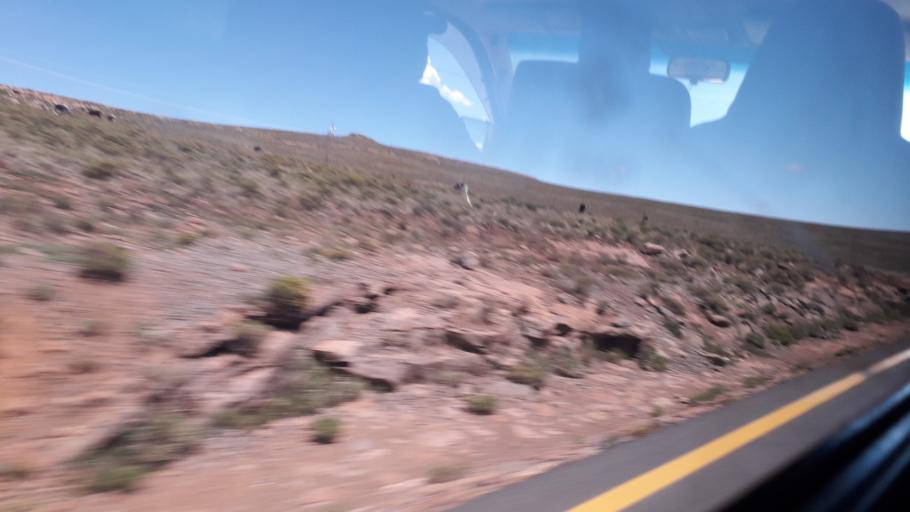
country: LS
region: Mokhotlong
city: Mokhotlong
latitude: -29.0581
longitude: 28.8521
